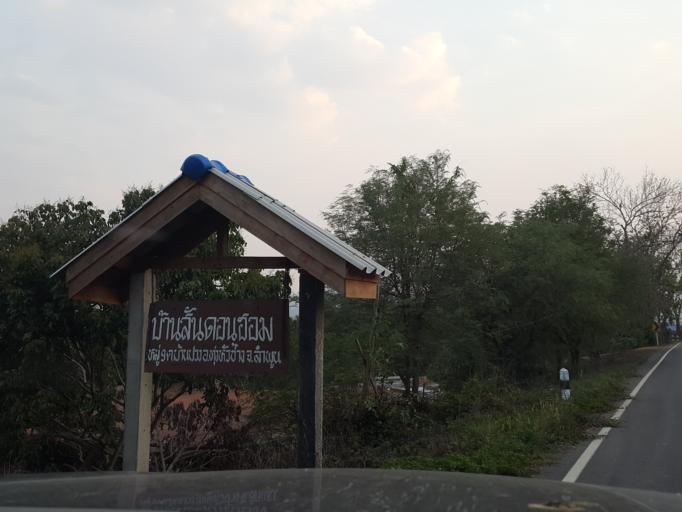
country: TH
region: Lamphun
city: Thung Hua Chang
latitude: 17.8715
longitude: 99.0767
